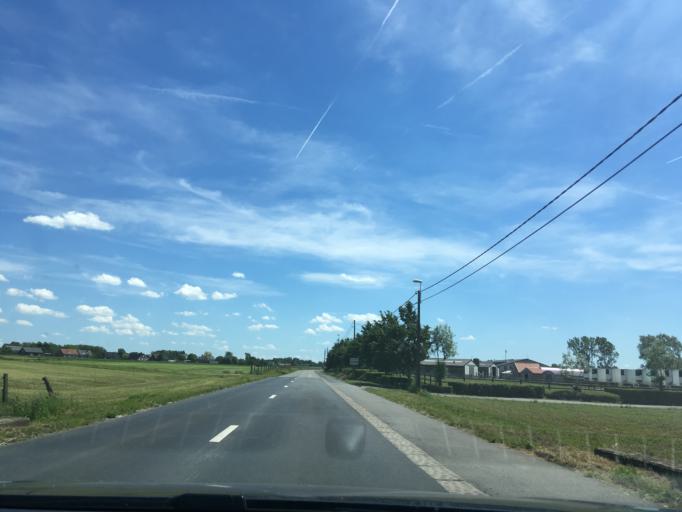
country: BE
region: Flanders
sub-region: Provincie West-Vlaanderen
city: Hooglede
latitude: 51.0076
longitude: 3.0858
